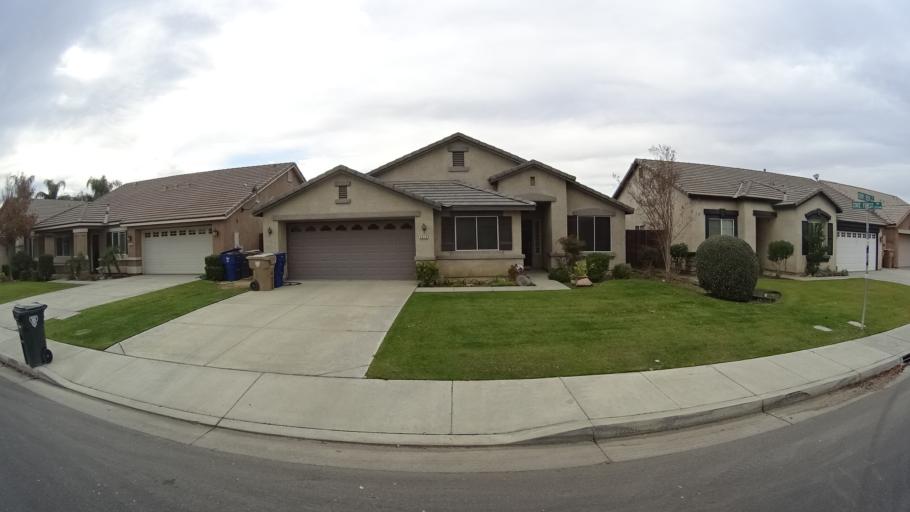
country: US
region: California
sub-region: Kern County
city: Rosedale
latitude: 35.4084
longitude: -119.1462
